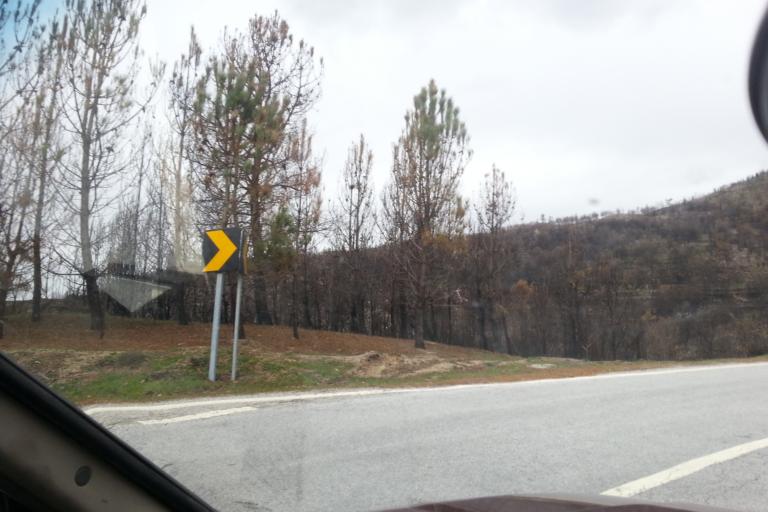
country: PT
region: Guarda
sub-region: Manteigas
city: Manteigas
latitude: 40.4687
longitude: -7.5899
